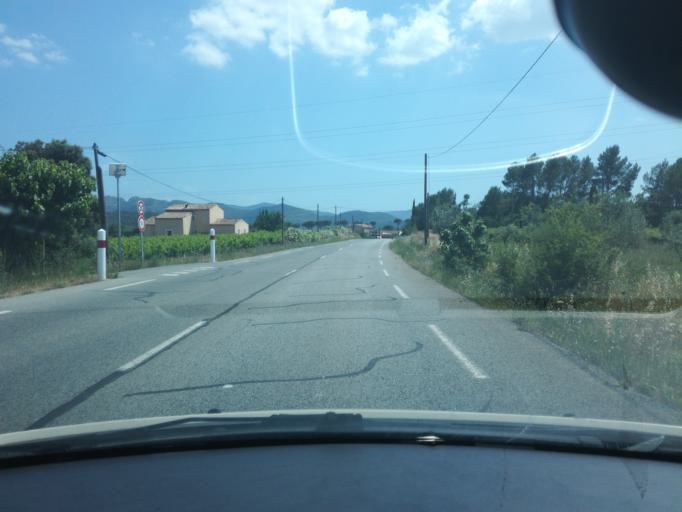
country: FR
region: Provence-Alpes-Cote d'Azur
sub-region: Departement du Var
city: Le Muy
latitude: 43.4972
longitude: 6.5656
